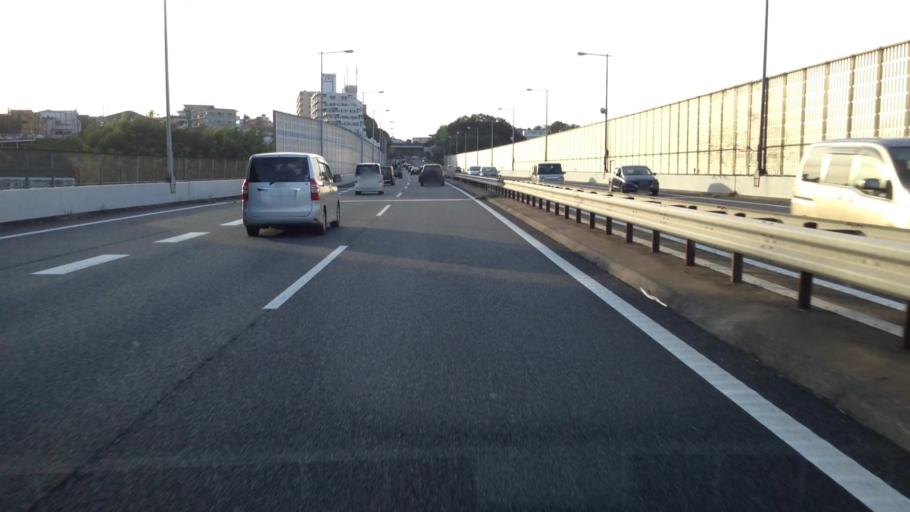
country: JP
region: Kanagawa
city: Kamakura
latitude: 35.3847
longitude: 139.5816
